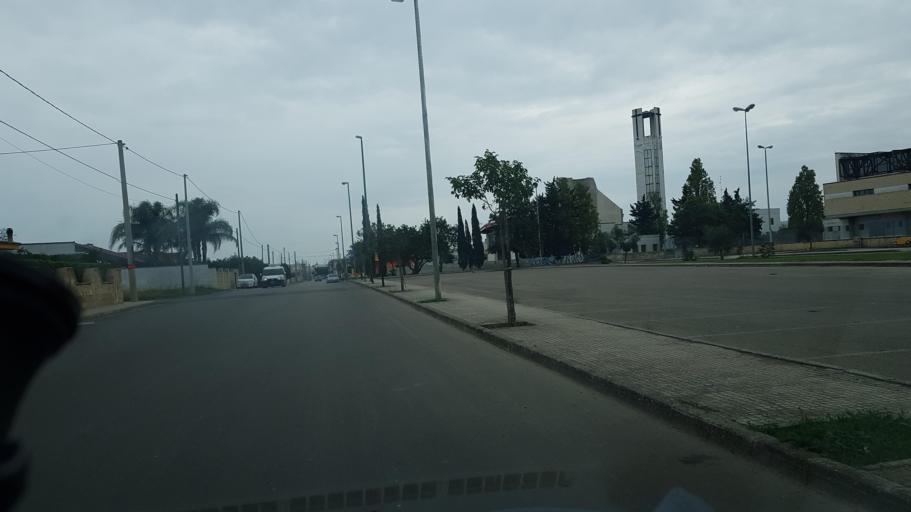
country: IT
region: Apulia
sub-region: Provincia di Lecce
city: Veglie
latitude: 40.3386
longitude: 17.9534
